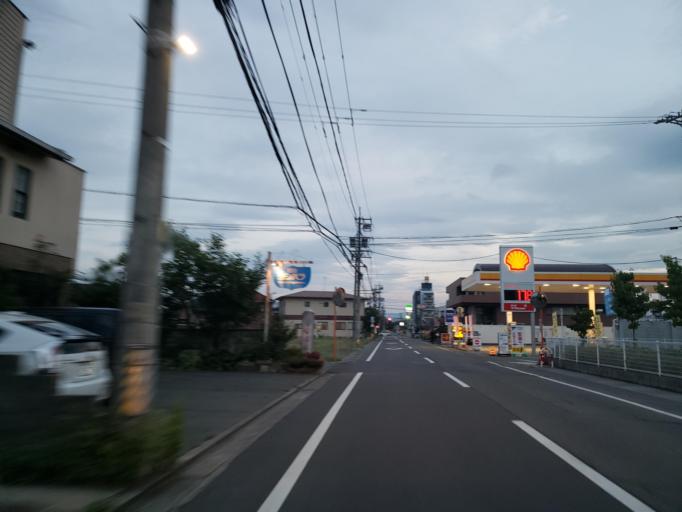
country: JP
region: Nagano
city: Nagano-shi
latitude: 36.6349
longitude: 138.1729
